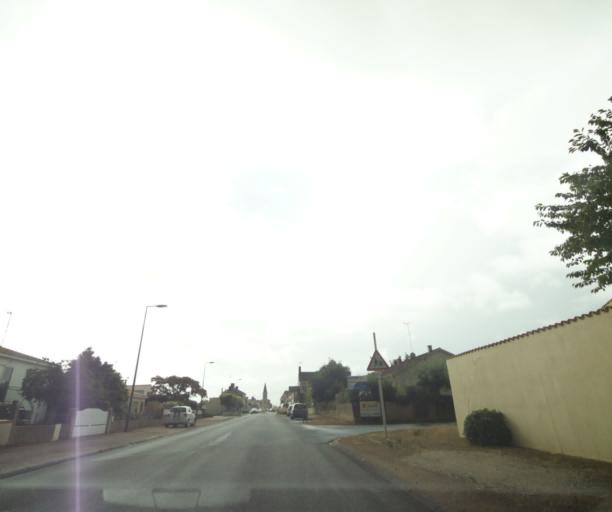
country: FR
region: Pays de la Loire
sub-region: Departement de la Vendee
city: Avrille
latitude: 46.4716
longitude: -1.4997
